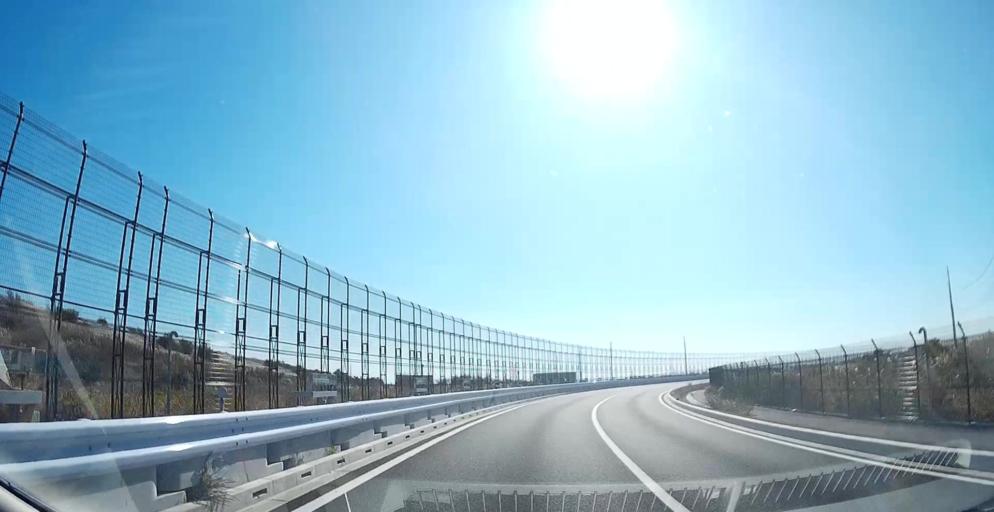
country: JP
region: Tokyo
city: Urayasu
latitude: 35.5945
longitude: 139.8092
